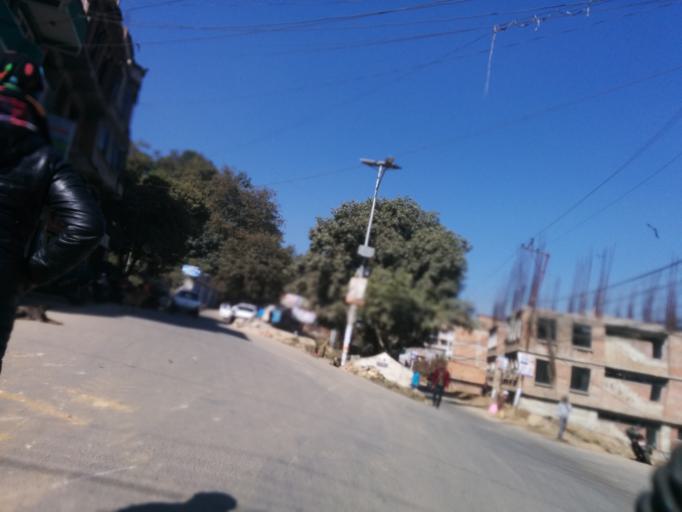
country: NP
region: Central Region
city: Kirtipur
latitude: 27.6774
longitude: 85.2807
